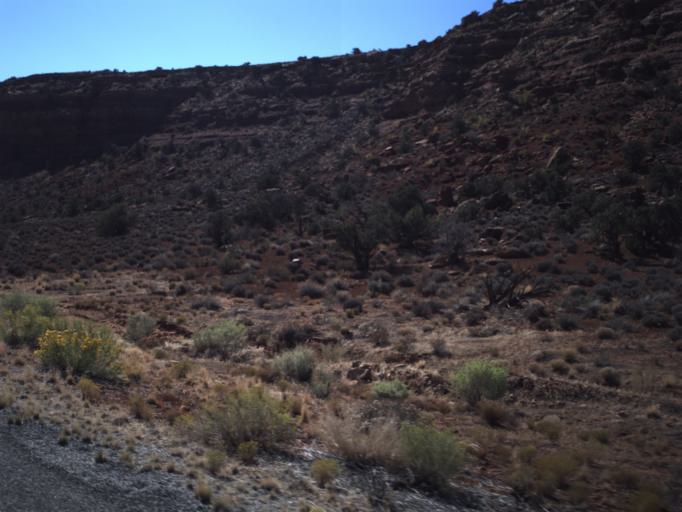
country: US
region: Utah
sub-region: San Juan County
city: Blanding
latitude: 37.7142
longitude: -110.2449
